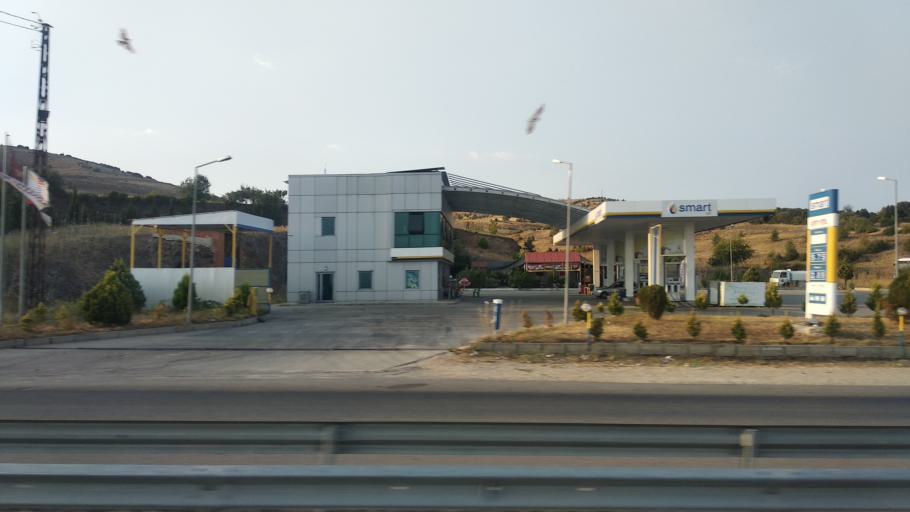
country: TR
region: Manisa
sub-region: Kula
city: Kula
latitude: 38.5678
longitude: 28.5725
